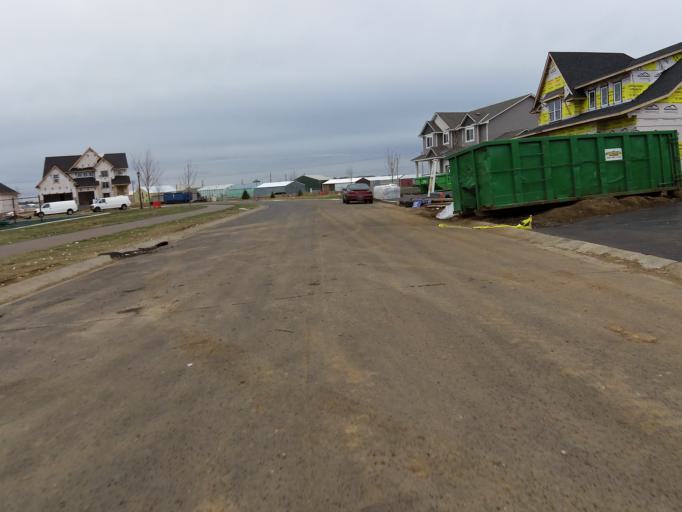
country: US
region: Minnesota
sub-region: Washington County
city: Lake Elmo
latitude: 44.9975
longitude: -92.8650
